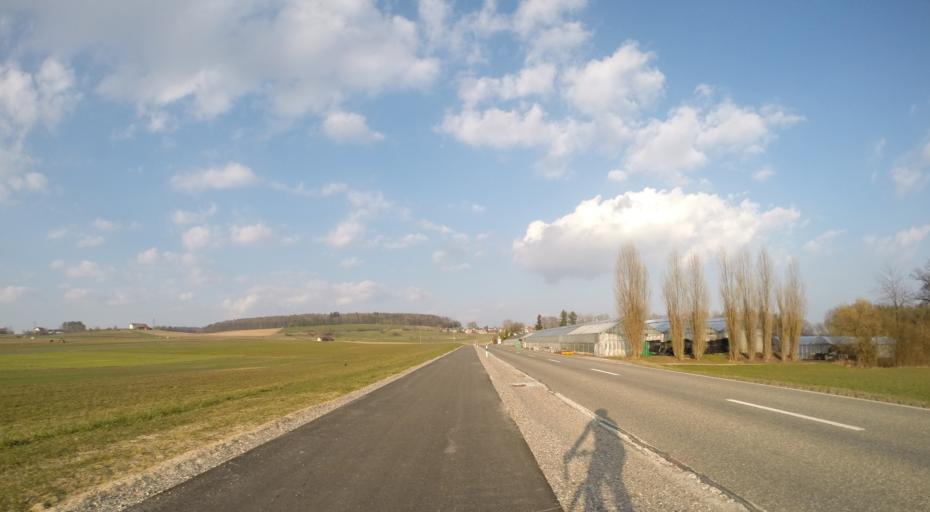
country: CH
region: Thurgau
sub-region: Frauenfeld District
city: Pfyn
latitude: 47.6187
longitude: 8.9253
